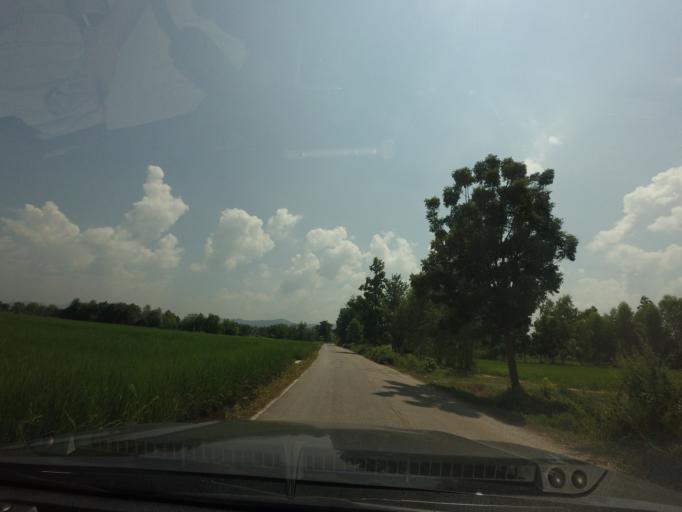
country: TH
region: Uttaradit
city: Thong Saen Khan
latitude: 17.4503
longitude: 100.3118
